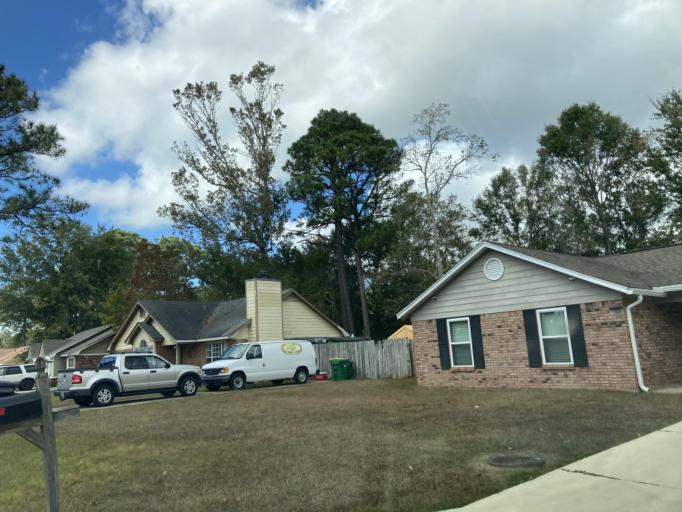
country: US
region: Mississippi
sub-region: Jackson County
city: Gulf Hills
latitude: 30.4470
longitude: -88.8264
